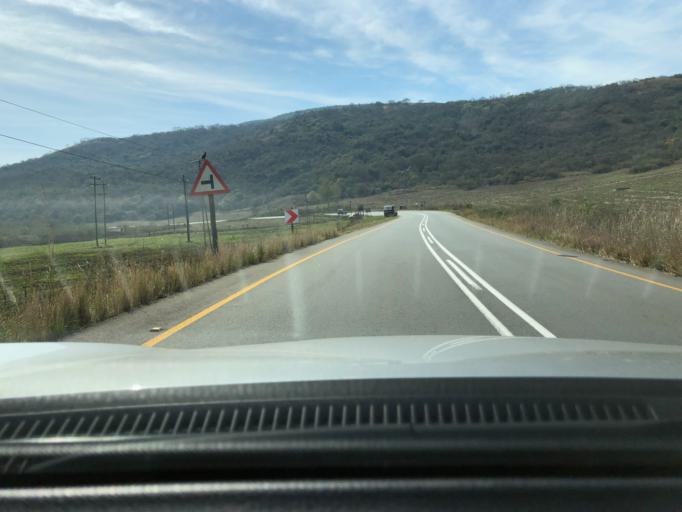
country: ZA
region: KwaZulu-Natal
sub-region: uMgungundlovu District Municipality
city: Richmond
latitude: -29.9704
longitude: 30.2528
